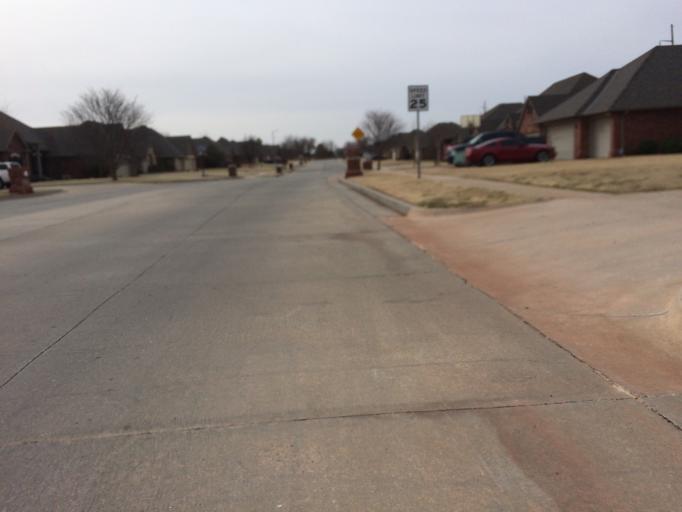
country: US
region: Oklahoma
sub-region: Cleveland County
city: Hall Park
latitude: 35.2180
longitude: -97.3965
